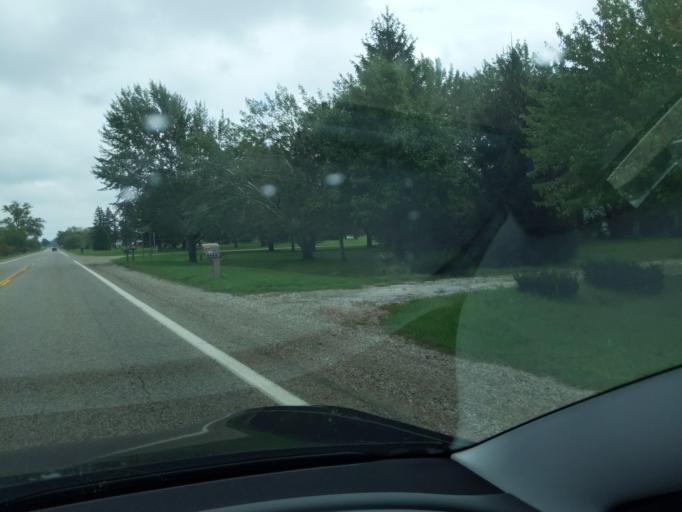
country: US
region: Michigan
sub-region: Eaton County
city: Charlotte
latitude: 42.5531
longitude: -84.7800
